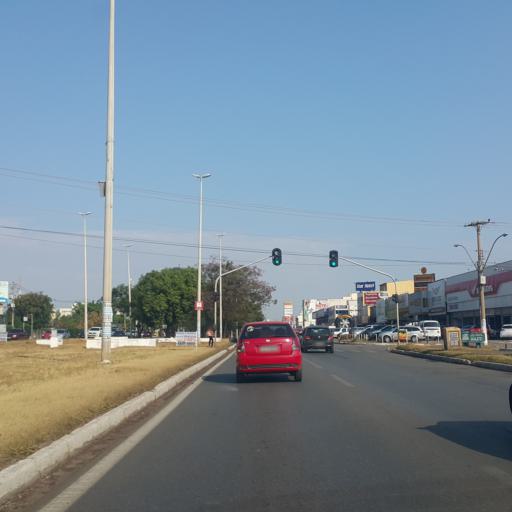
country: BR
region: Federal District
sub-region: Brasilia
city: Brasilia
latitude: -15.8524
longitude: -48.0405
